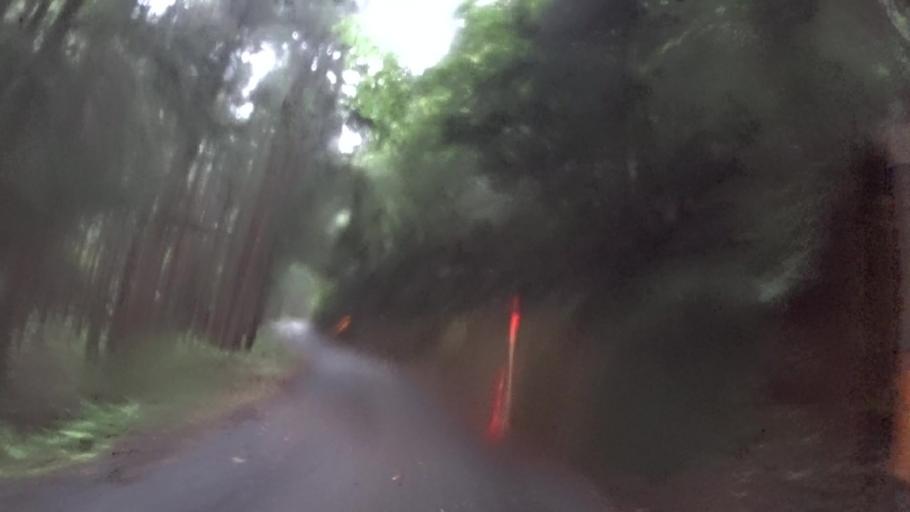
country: JP
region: Shiga Prefecture
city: Kitahama
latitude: 35.2675
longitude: 135.8023
